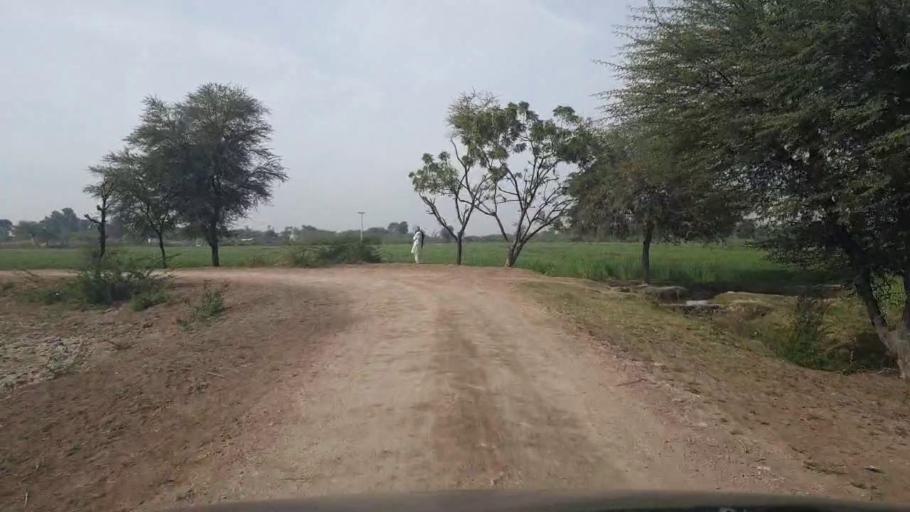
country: PK
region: Sindh
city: Umarkot
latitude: 25.3593
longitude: 69.6655
